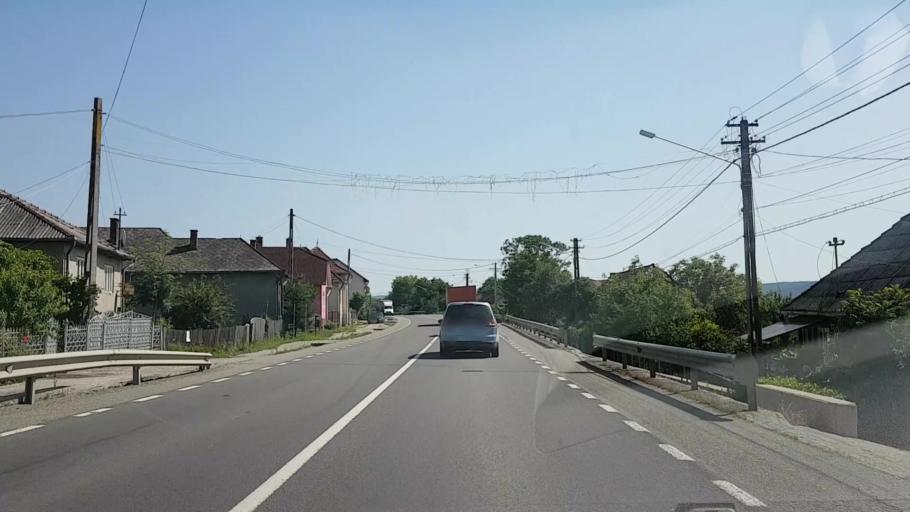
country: RO
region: Bistrita-Nasaud
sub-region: Comuna Sieu-Odorhei
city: Sieu-Odorhei
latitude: 47.1415
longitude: 24.3068
